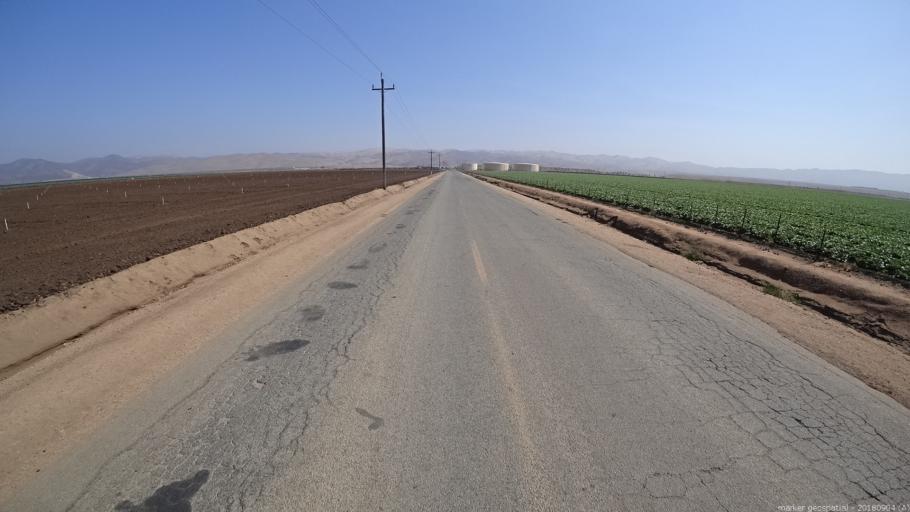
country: US
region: California
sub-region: Monterey County
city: Gonzales
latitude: 36.5236
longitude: -121.4224
